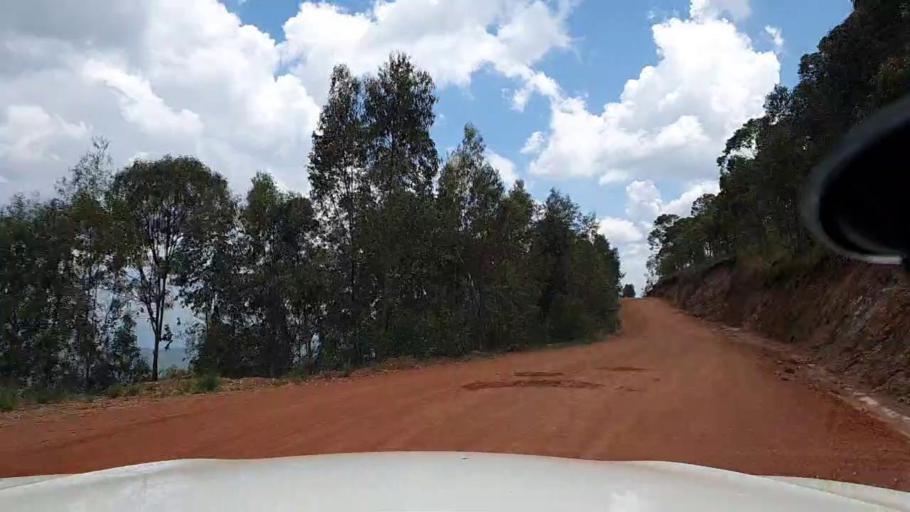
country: RW
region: Kigali
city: Kigali
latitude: -1.7854
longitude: 29.8451
